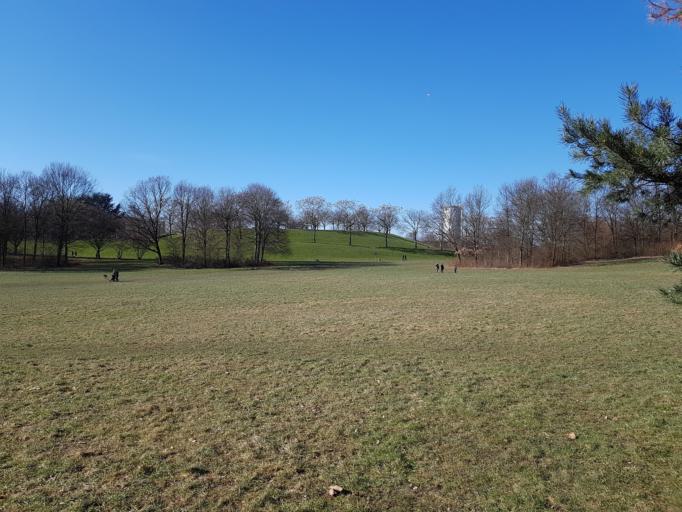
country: DE
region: North Rhine-Westphalia
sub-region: Regierungsbezirk Koln
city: Konigswinter
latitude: 50.7066
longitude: 7.1510
